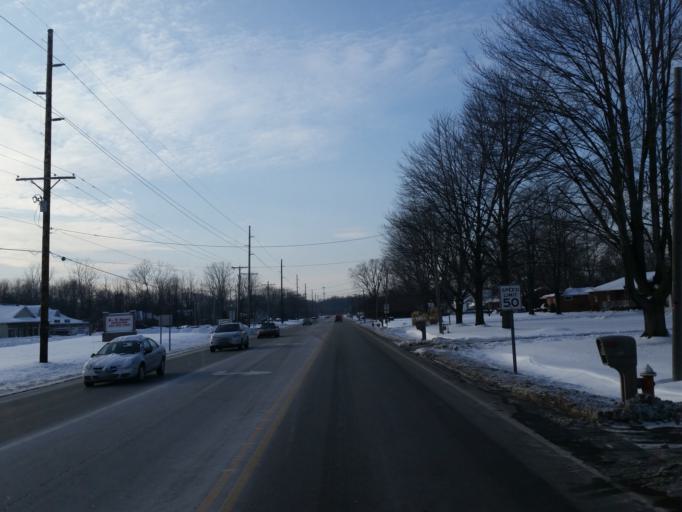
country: US
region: Ohio
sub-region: Lorain County
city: Sheffield Lake
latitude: 41.4612
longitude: -82.1139
